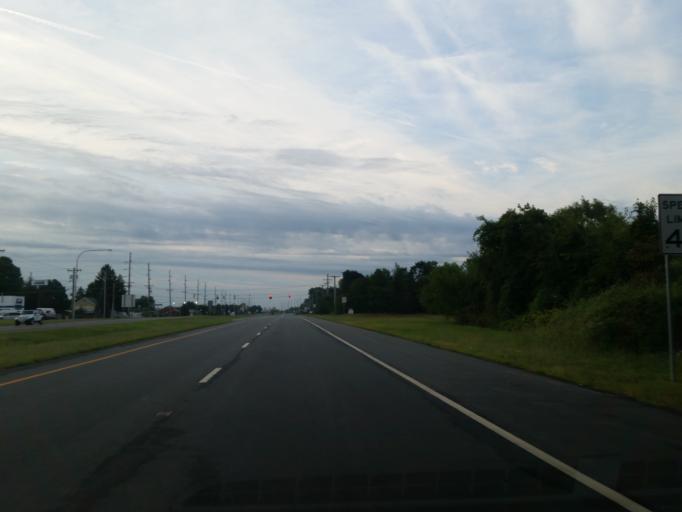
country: US
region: Delaware
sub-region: Kent County
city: Dover Base Housing
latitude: 39.1418
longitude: -75.4978
